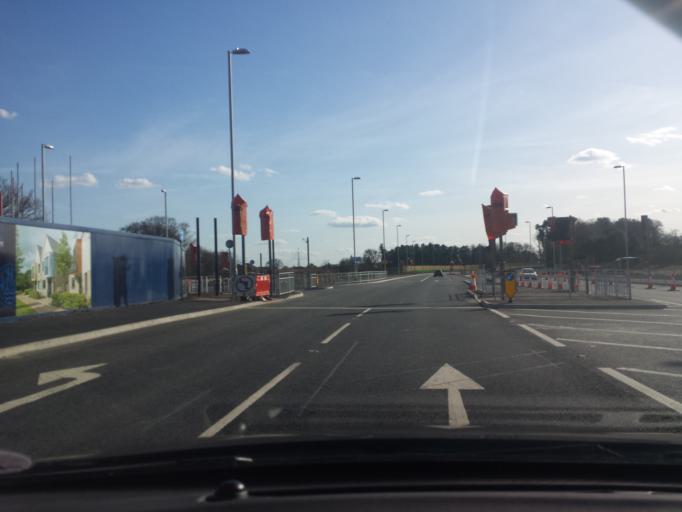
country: GB
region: England
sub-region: Essex
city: Colchester
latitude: 51.9196
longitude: 0.9034
